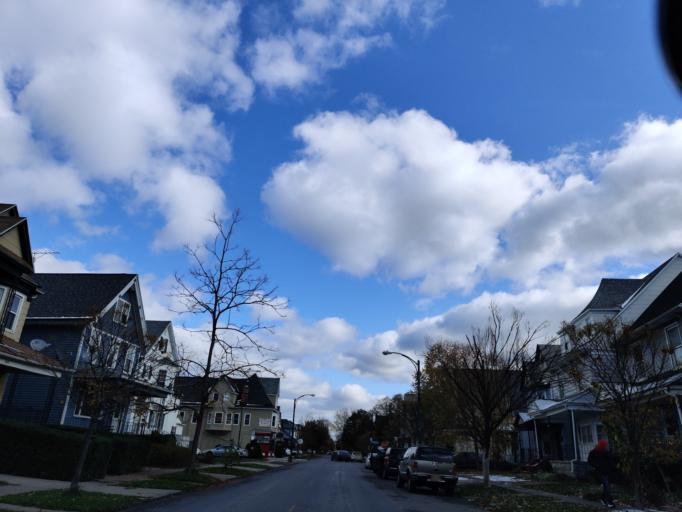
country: US
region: New York
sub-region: Erie County
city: Buffalo
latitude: 42.9221
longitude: -78.8886
